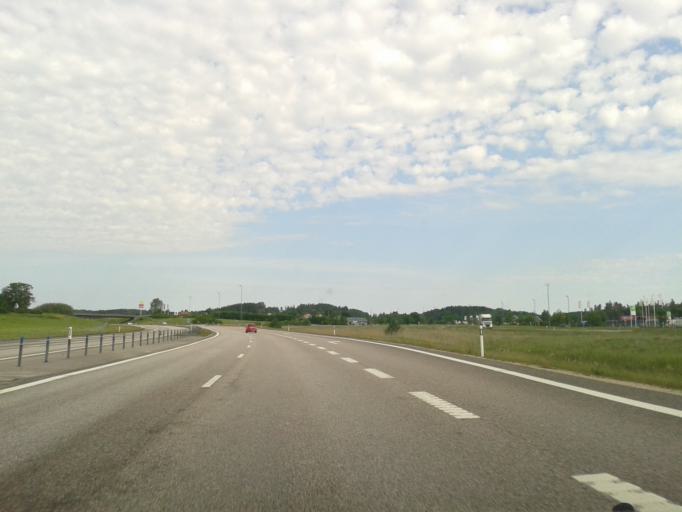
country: SE
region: Vaestra Goetaland
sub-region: Munkedals Kommun
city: Munkedal
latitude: 58.4855
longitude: 11.6295
